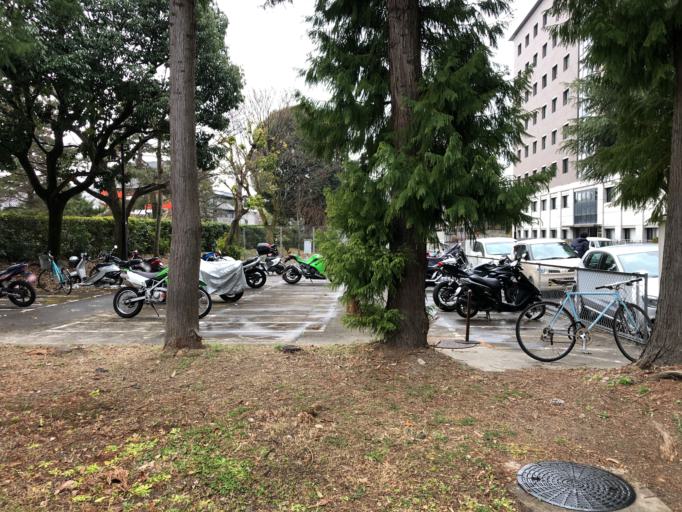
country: JP
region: Kyoto
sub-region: Kyoto-shi
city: Kamigyo-ku
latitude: 35.0255
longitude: 135.7826
